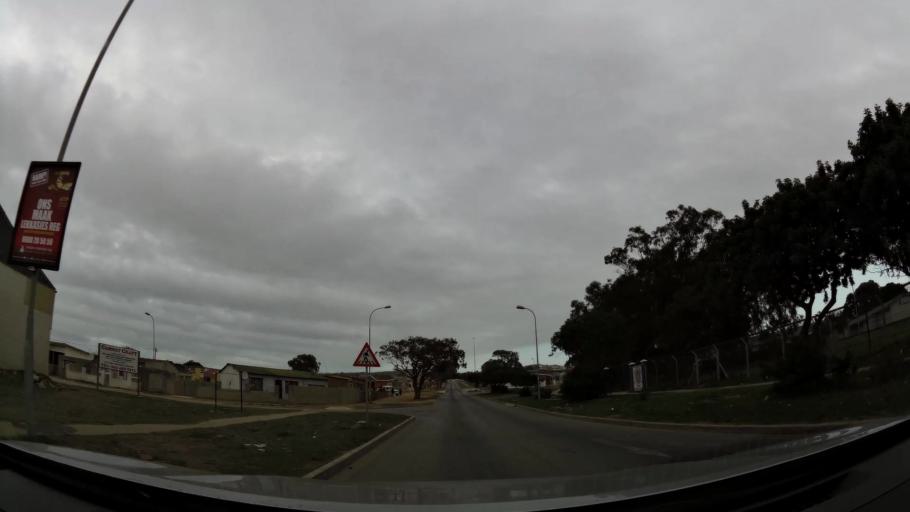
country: ZA
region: Eastern Cape
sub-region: Nelson Mandela Bay Metropolitan Municipality
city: Port Elizabeth
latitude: -33.9107
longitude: 25.5571
